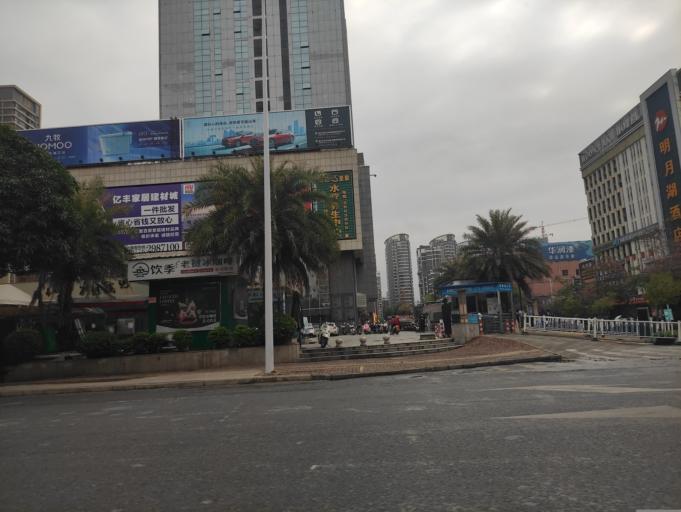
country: CN
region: Guangxi Zhuangzu Zizhiqu
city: Baise City
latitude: 23.8916
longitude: 106.6303
